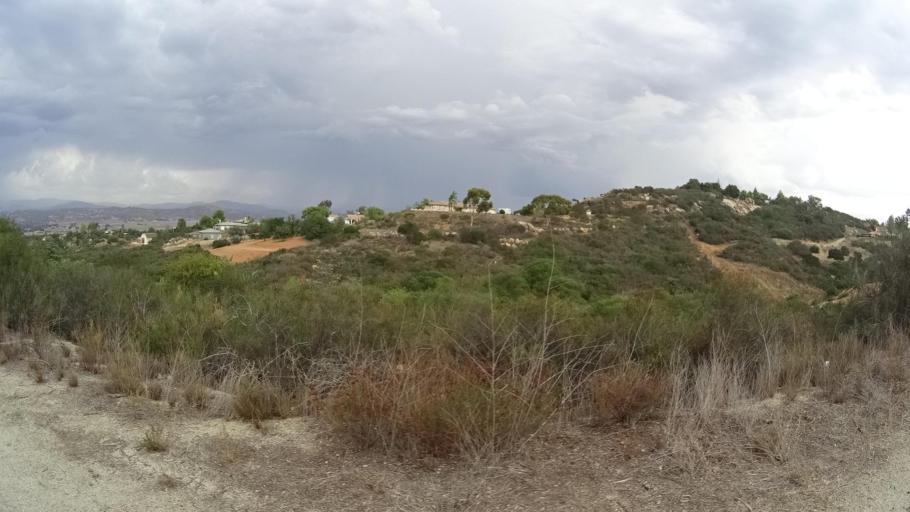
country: US
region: California
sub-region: San Diego County
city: San Pasqual
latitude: 33.0226
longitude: -116.9547
